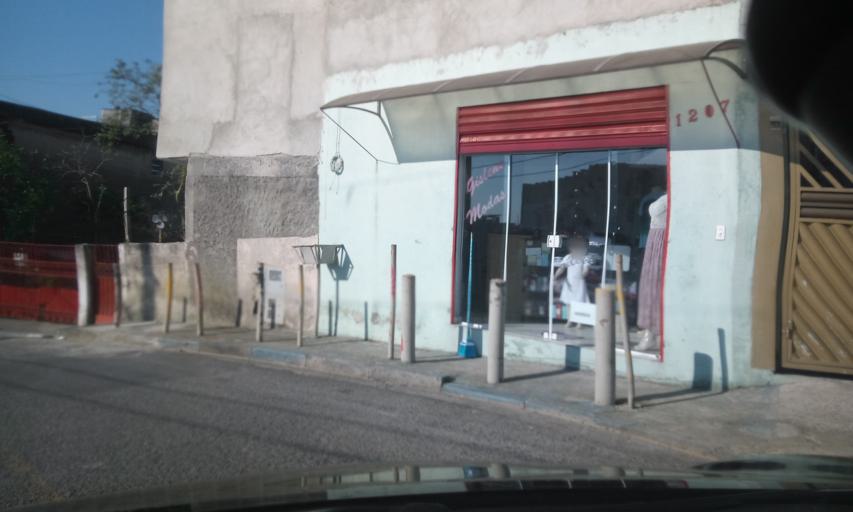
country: BR
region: Sao Paulo
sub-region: Sao Bernardo Do Campo
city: Sao Bernardo do Campo
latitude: -23.7921
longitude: -46.5301
